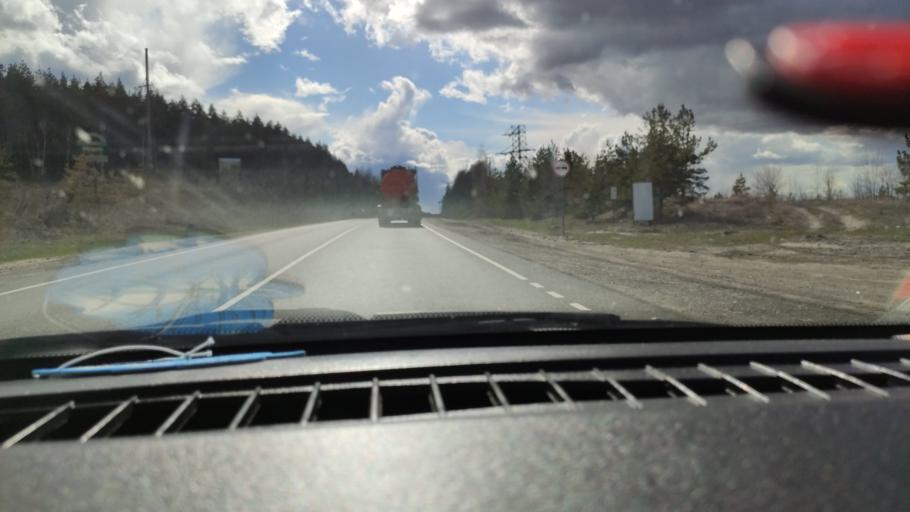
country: RU
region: Saratov
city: Khvalynsk
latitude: 52.5410
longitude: 48.0560
